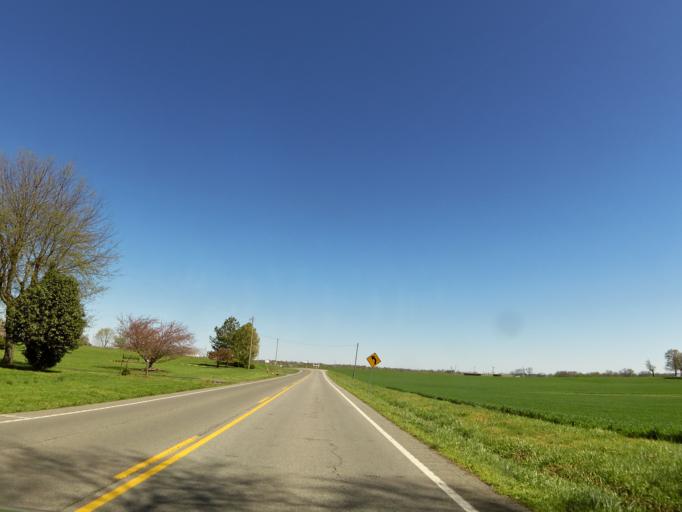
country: US
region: Tennessee
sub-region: Robertson County
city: Springfield
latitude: 36.6440
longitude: -86.8543
